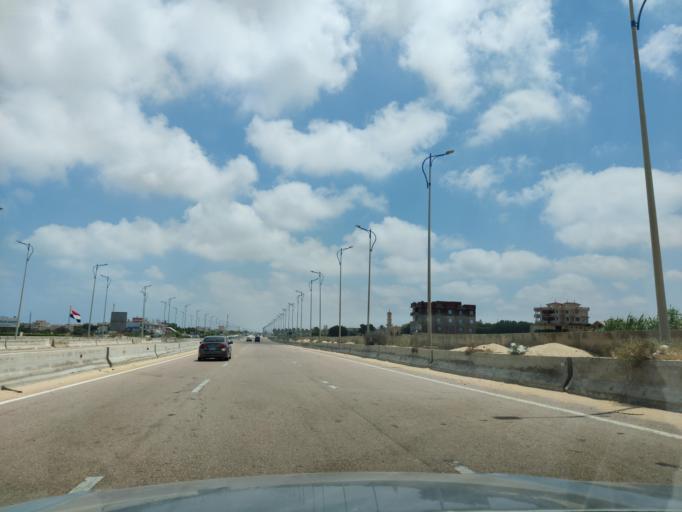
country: EG
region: Alexandria
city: Alexandria
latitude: 30.9751
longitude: 29.5704
